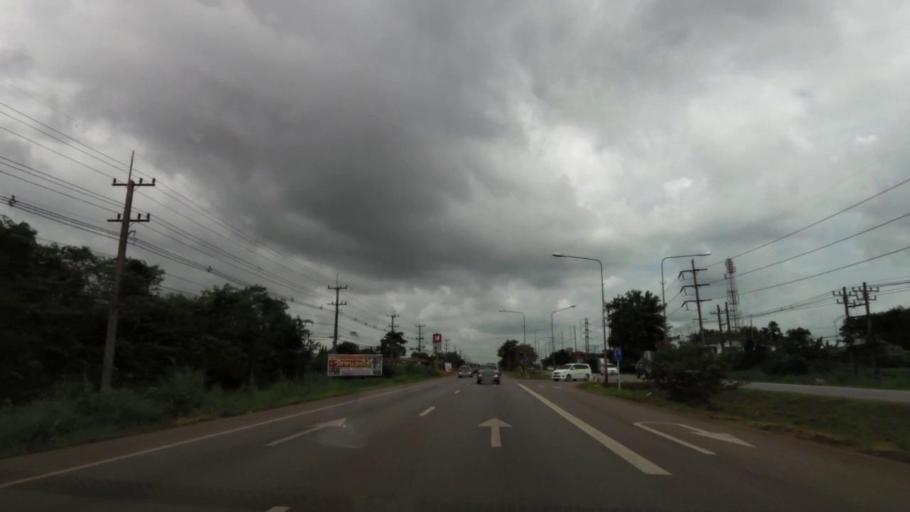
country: TH
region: Chanthaburi
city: Na Yai Am
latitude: 12.7767
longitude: 101.8312
